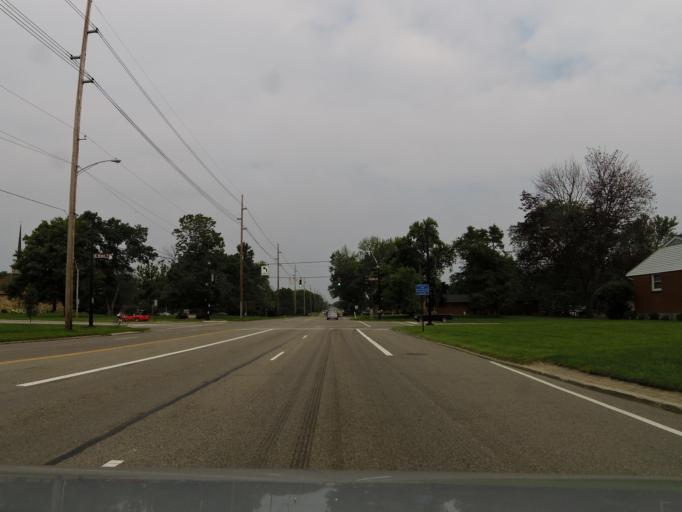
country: US
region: Ohio
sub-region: Greene County
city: Bellbrook
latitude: 39.6706
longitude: -84.1117
